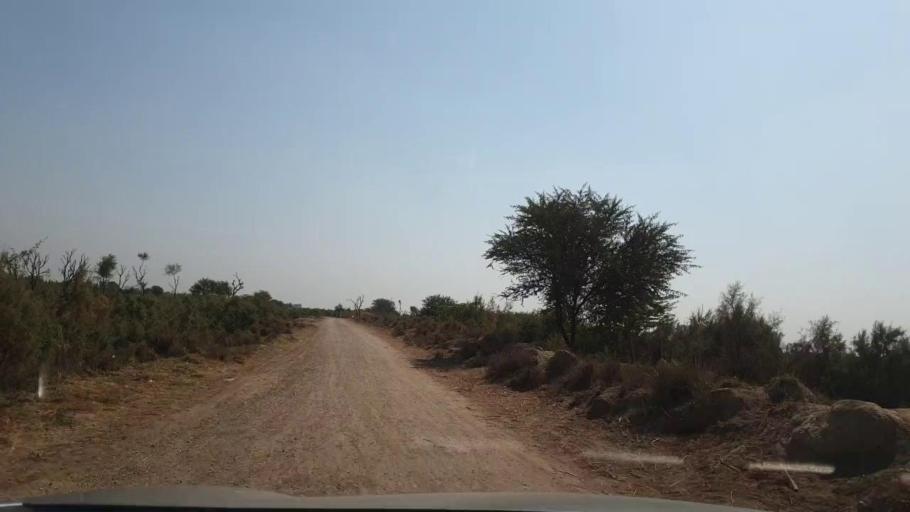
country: PK
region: Sindh
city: Berani
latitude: 25.6319
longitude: 68.8634
